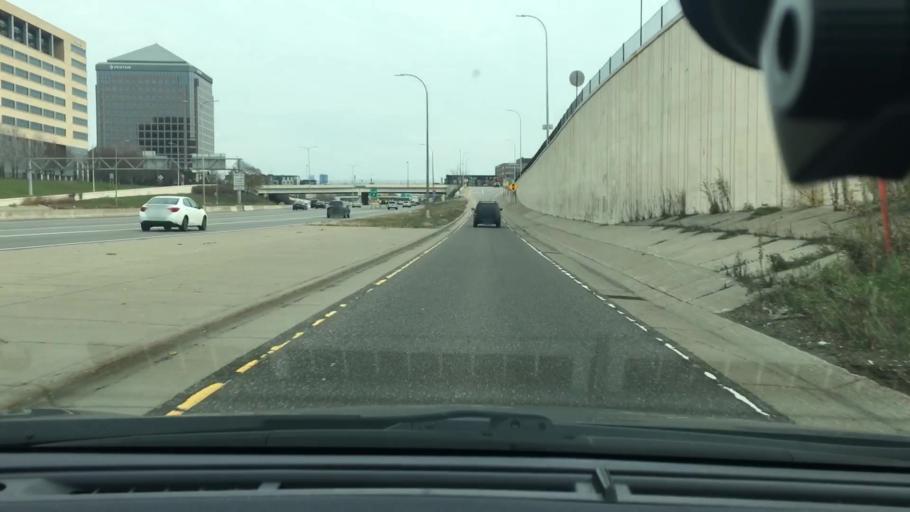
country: US
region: Minnesota
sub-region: Hennepin County
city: Saint Louis Park
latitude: 44.9702
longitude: -93.3560
